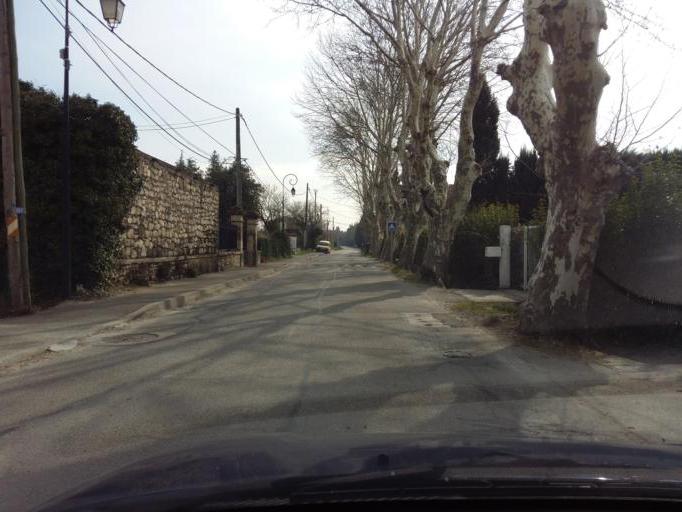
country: FR
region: Provence-Alpes-Cote d'Azur
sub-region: Departement des Bouches-du-Rhone
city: Noves
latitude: 43.8739
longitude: 4.9035
